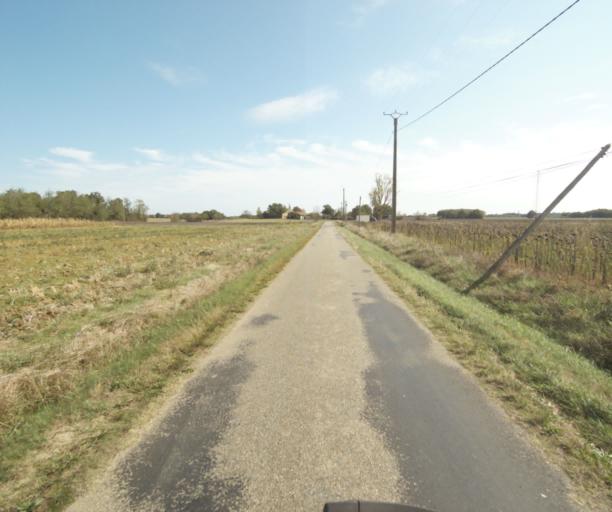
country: FR
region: Midi-Pyrenees
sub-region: Departement du Tarn-et-Garonne
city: Verdun-sur-Garonne
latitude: 43.8435
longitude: 1.1778
